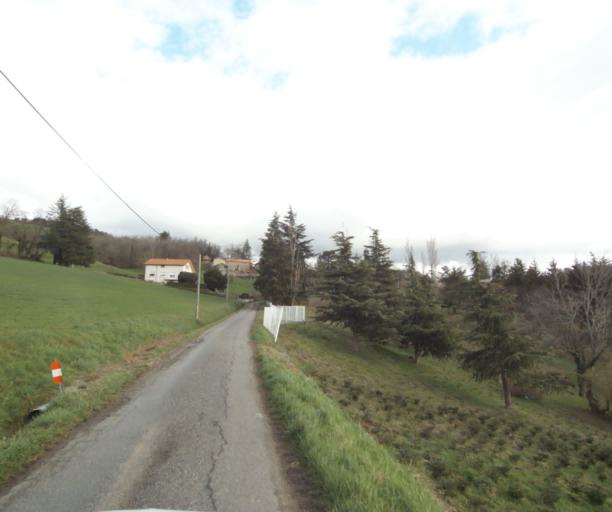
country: FR
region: Rhone-Alpes
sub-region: Departement de la Loire
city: La Talaudiere
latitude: 45.4905
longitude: 4.4161
